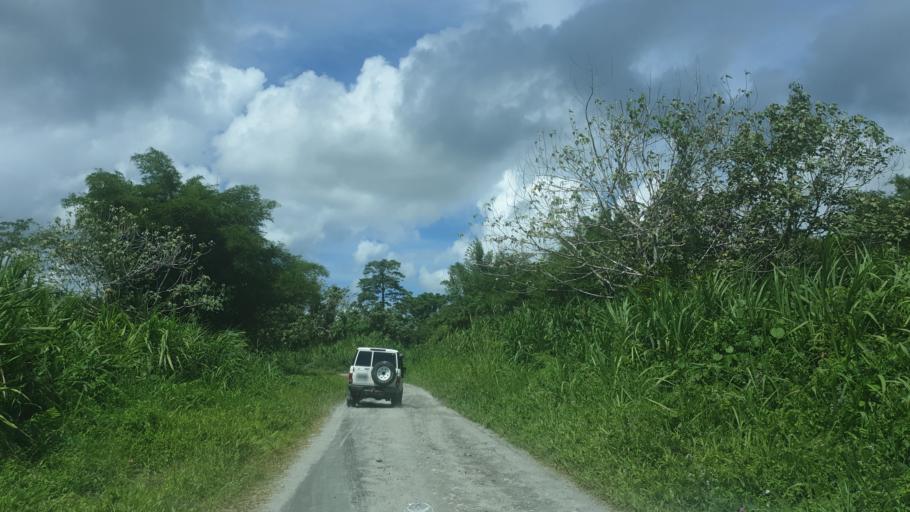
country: PG
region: Bougainville
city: Panguna
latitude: -6.7382
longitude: 155.5015
